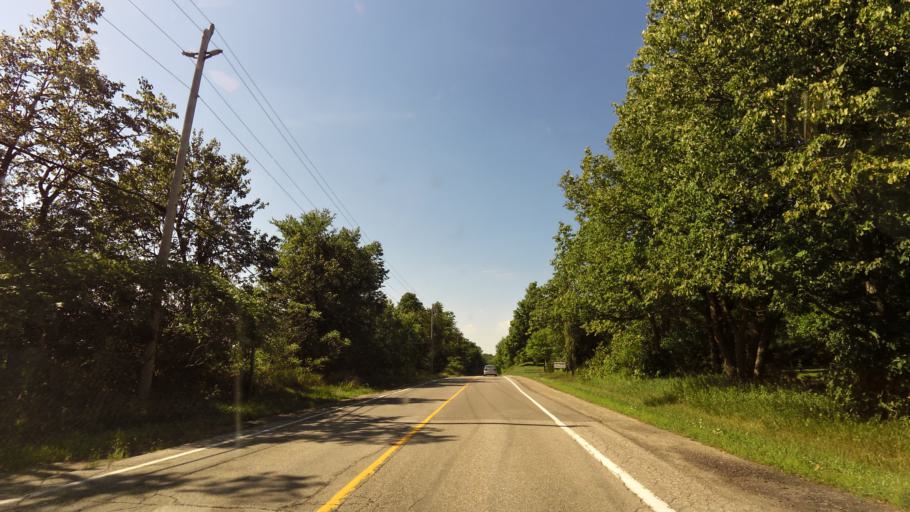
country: CA
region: Ontario
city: Orangeville
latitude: 43.7921
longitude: -80.0004
